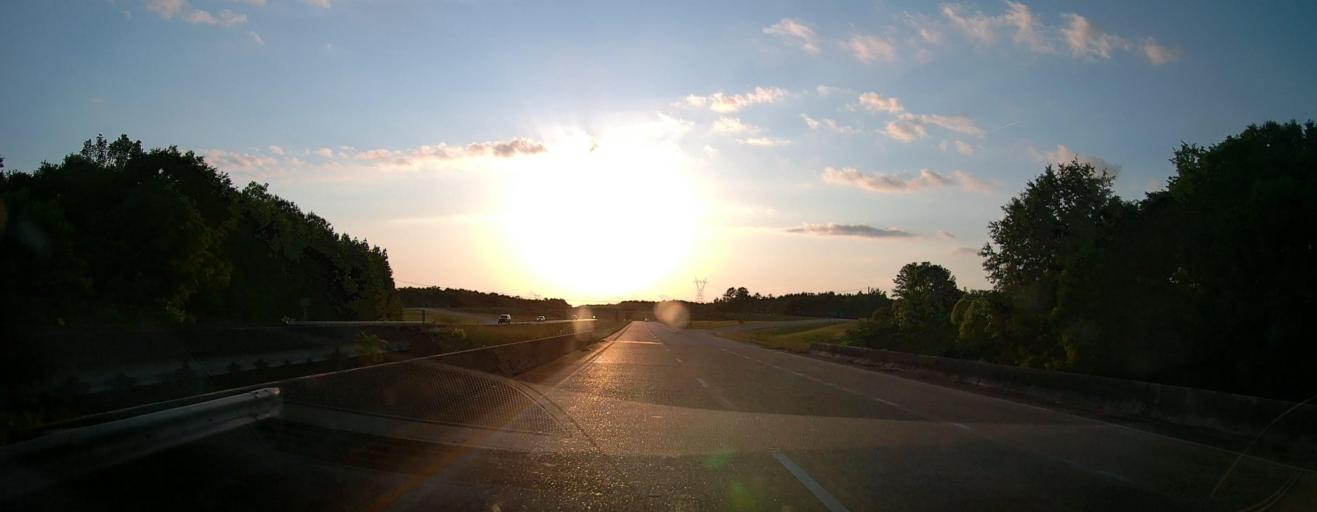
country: US
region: Mississippi
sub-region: Lee County
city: Plantersville
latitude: 34.2756
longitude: -88.6337
